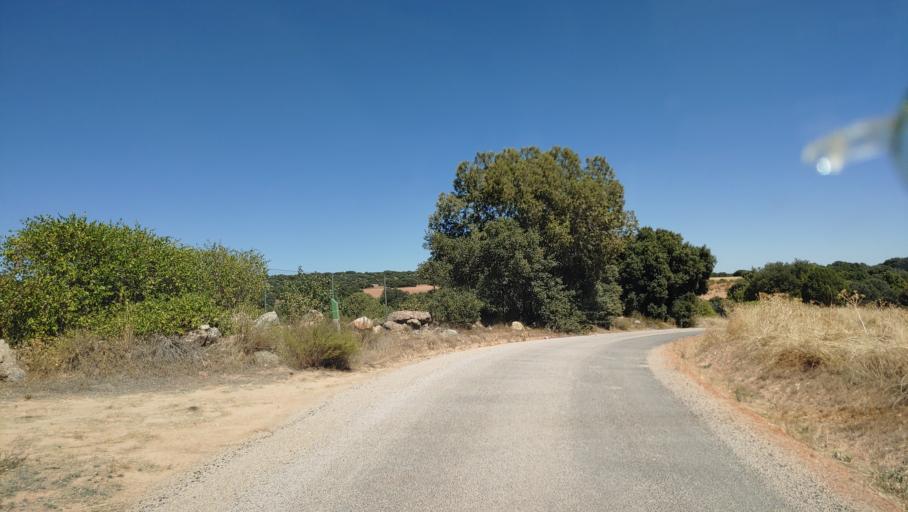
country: ES
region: Castille-La Mancha
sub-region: Provincia de Albacete
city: Ossa de Montiel
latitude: 38.9289
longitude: -2.7813
